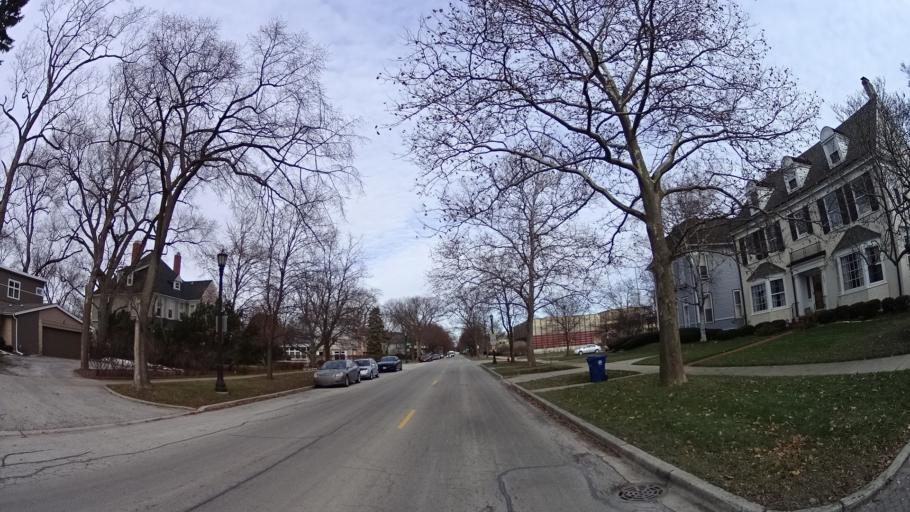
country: US
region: Illinois
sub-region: Cook County
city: Evanston
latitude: 42.0452
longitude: -87.6902
